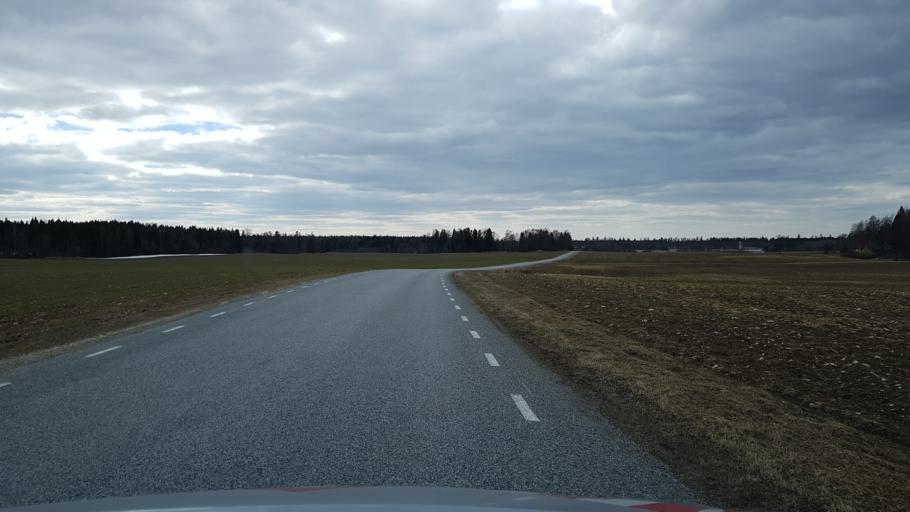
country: EE
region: Laeaene-Virumaa
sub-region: Kadrina vald
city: Kadrina
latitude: 59.2462
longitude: 26.2063
